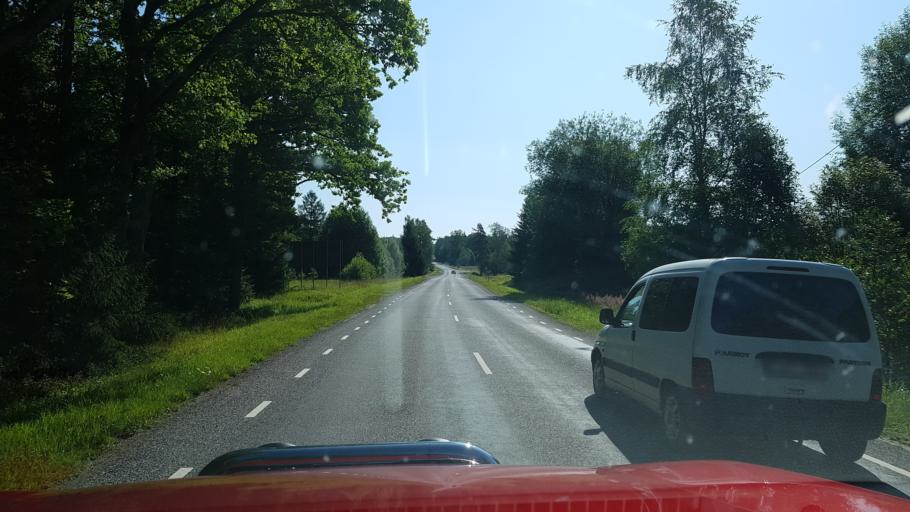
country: EE
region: Vorumaa
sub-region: Voru linn
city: Voru
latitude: 57.9761
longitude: 26.7863
